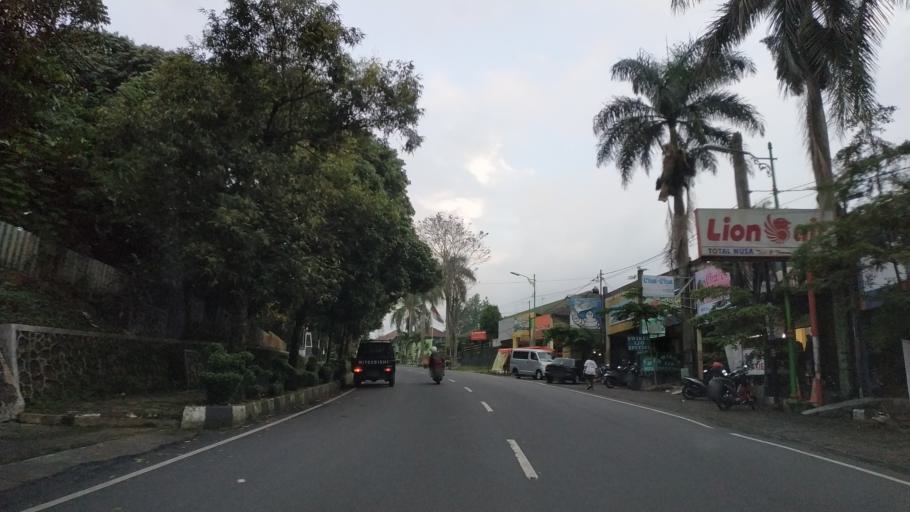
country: ID
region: Central Java
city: Salatiga
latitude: -7.3356
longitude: 110.5060
